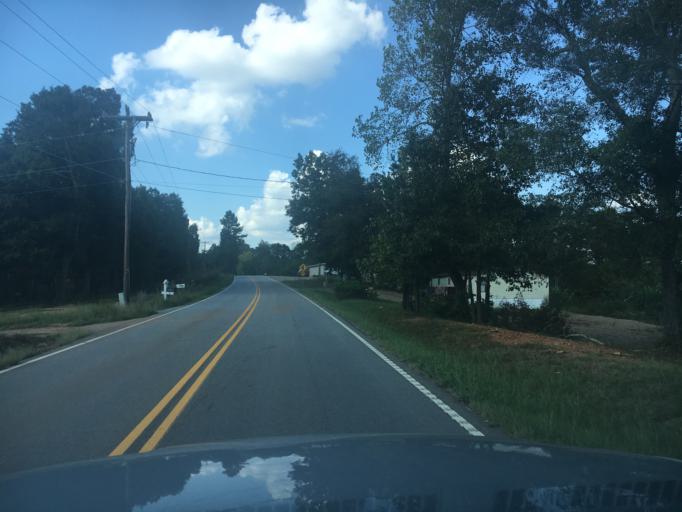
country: US
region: South Carolina
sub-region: Greenville County
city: Fountain Inn
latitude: 34.5695
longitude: -82.2162
